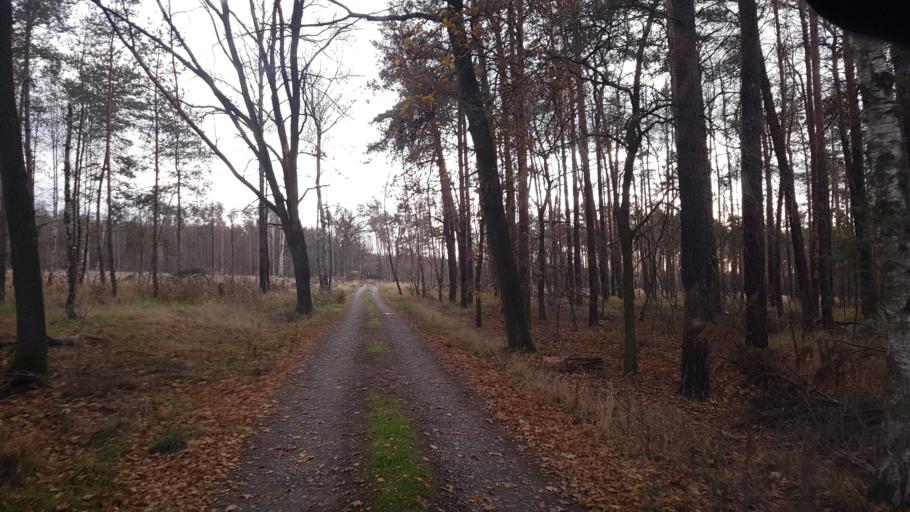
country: DE
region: Brandenburg
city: Falkenberg
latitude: 51.5684
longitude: 13.2832
